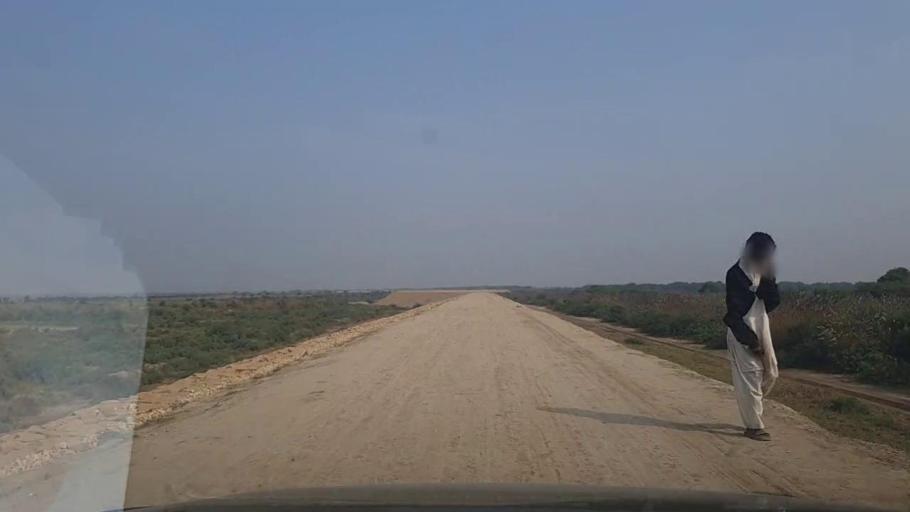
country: PK
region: Sindh
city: Bulri
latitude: 24.9538
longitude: 68.2906
